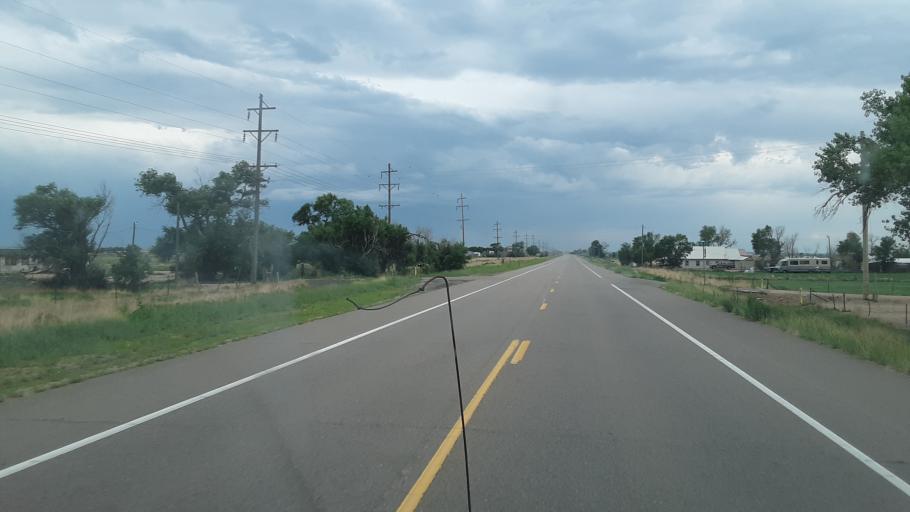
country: US
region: Colorado
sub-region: Crowley County
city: Ordway
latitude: 38.2074
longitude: -103.7482
